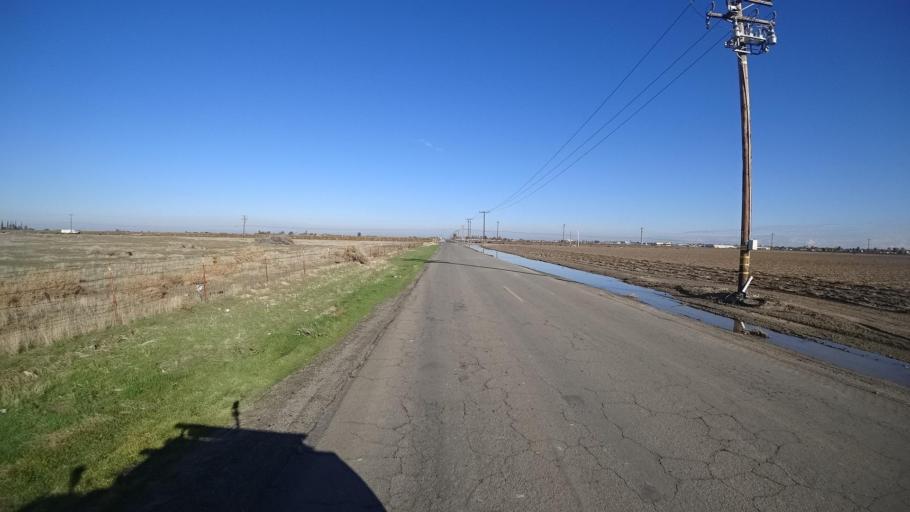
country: US
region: California
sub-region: Kern County
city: Delano
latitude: 35.7598
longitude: -119.2763
